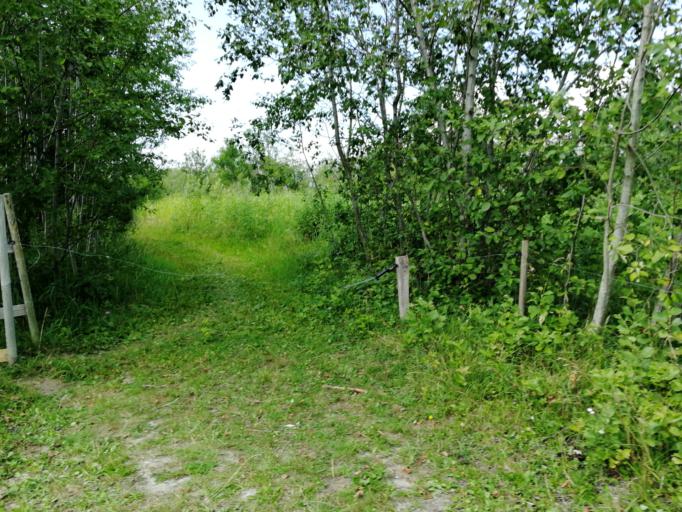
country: EE
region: Laeaene
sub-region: Lihula vald
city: Lihula
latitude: 58.7257
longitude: 23.8074
